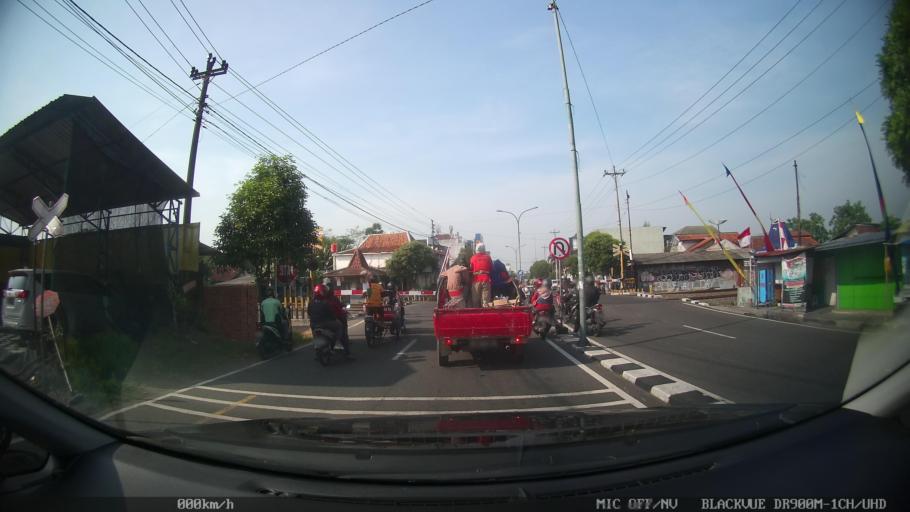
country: ID
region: Daerah Istimewa Yogyakarta
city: Yogyakarta
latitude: -7.7882
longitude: 110.3540
